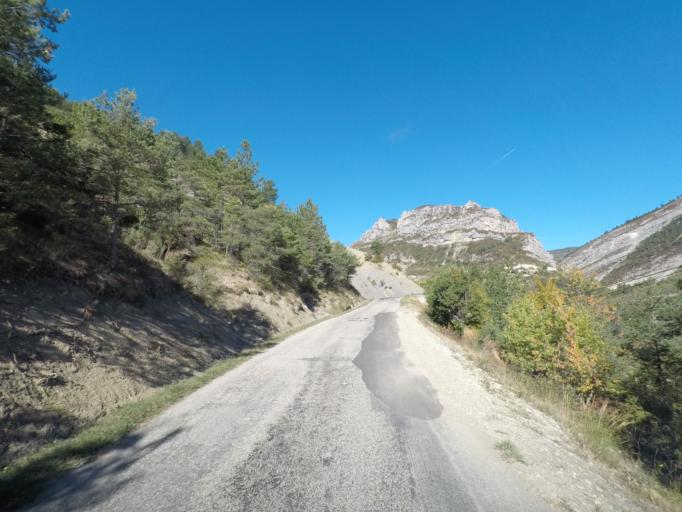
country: FR
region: Rhone-Alpes
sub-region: Departement de la Drome
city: Buis-les-Baronnies
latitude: 44.5017
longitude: 5.3517
